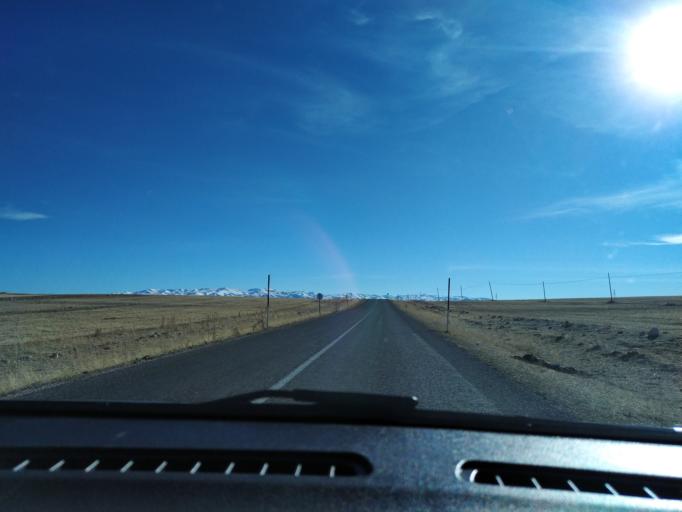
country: TR
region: Kayseri
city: Orensehir
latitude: 38.9747
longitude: 36.6742
